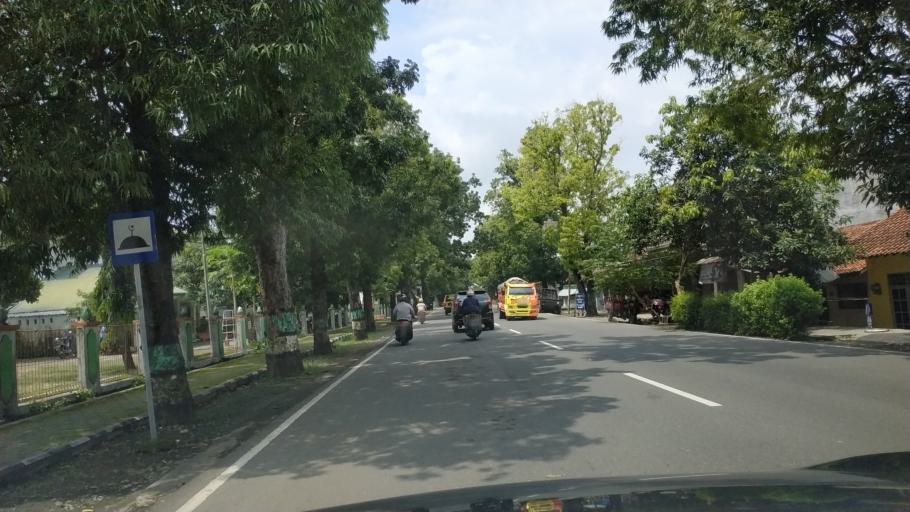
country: ID
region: Central Java
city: Slawi
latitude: -6.9803
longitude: 109.1281
